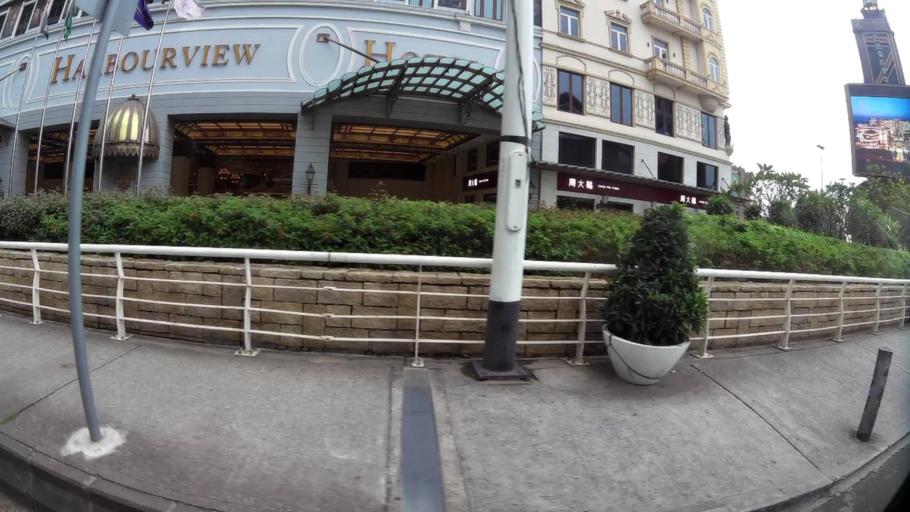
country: MO
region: Macau
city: Macau
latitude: 22.1903
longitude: 113.5558
